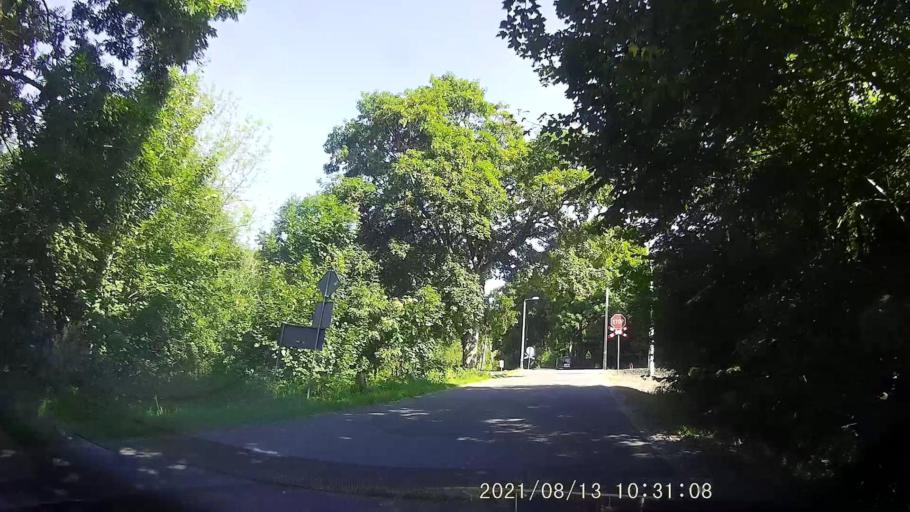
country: PL
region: Lower Silesian Voivodeship
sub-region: Powiat klodzki
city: Duszniki-Zdroj
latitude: 50.4112
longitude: 16.3803
